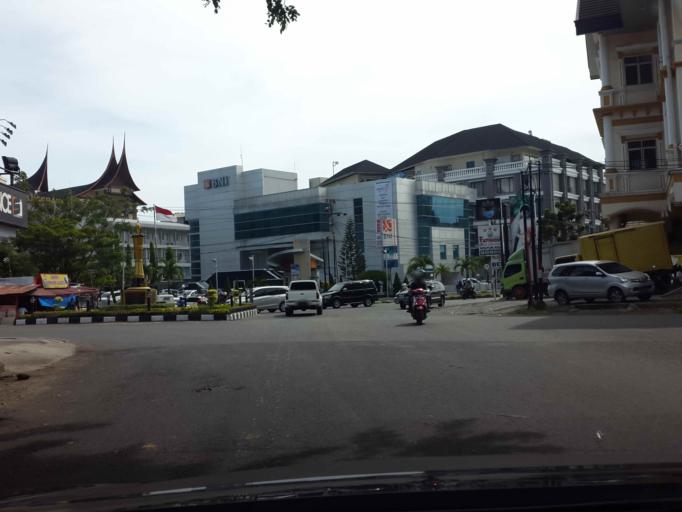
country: ID
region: West Sumatra
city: Padang
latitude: -0.9546
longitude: 100.3607
